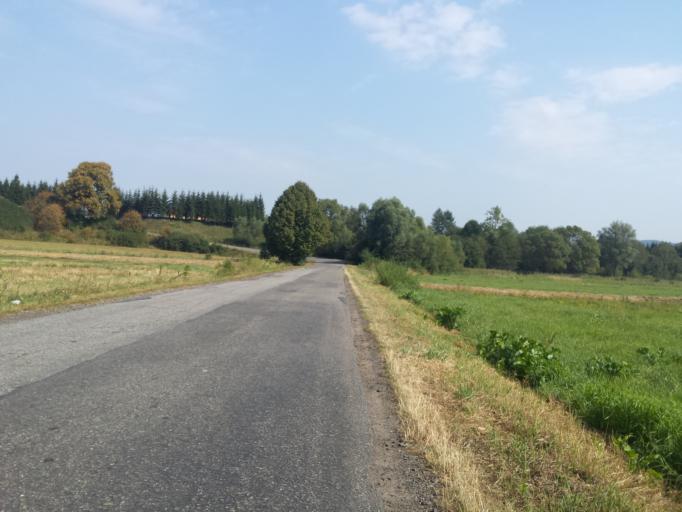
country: PL
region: Subcarpathian Voivodeship
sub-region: Powiat sanocki
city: Sanok
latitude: 49.6270
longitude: 22.2768
